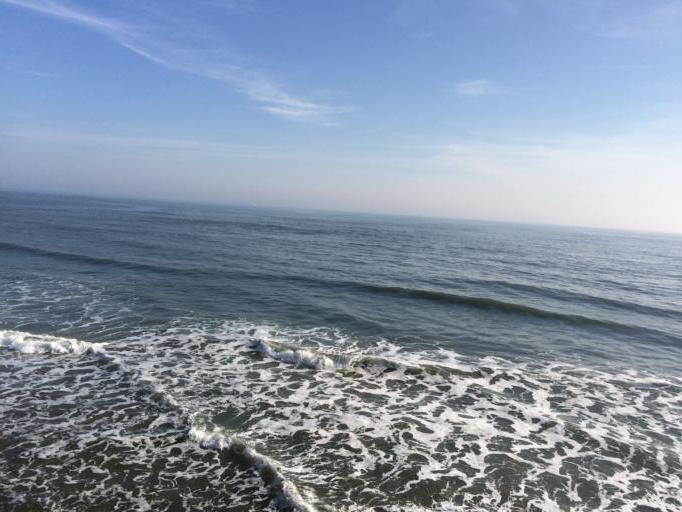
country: US
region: New Jersey
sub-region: Atlantic County
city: Atlantic City
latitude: 39.3525
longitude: -74.4337
